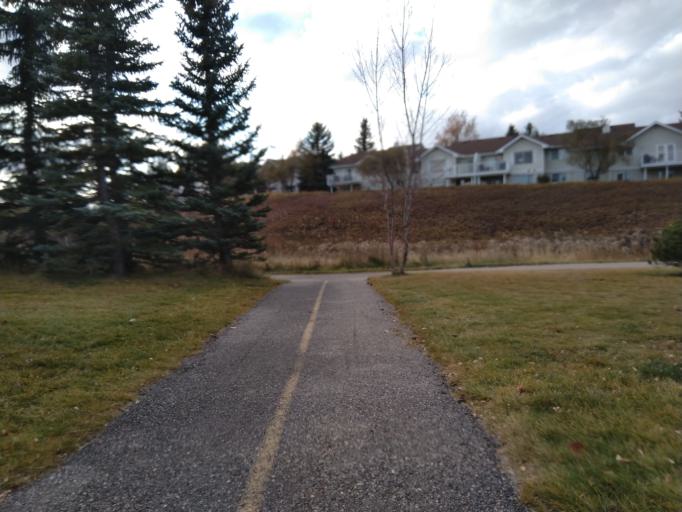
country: CA
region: Alberta
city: Calgary
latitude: 51.1432
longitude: -114.1160
